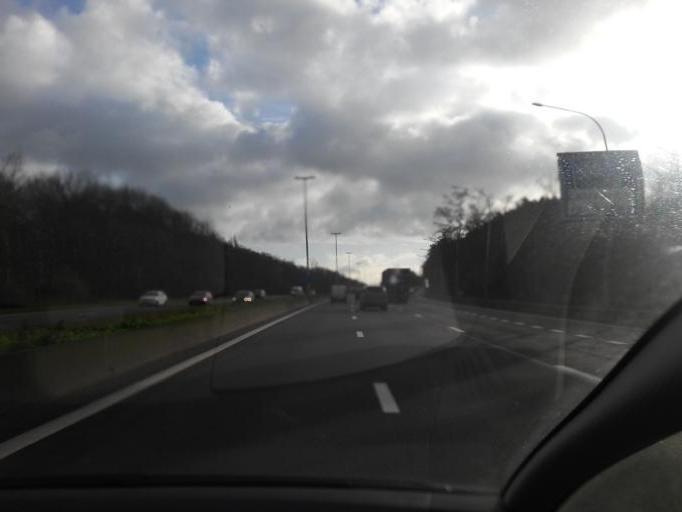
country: BE
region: Wallonia
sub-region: Province du Brabant Wallon
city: Wavre
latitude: 50.7051
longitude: 4.6112
